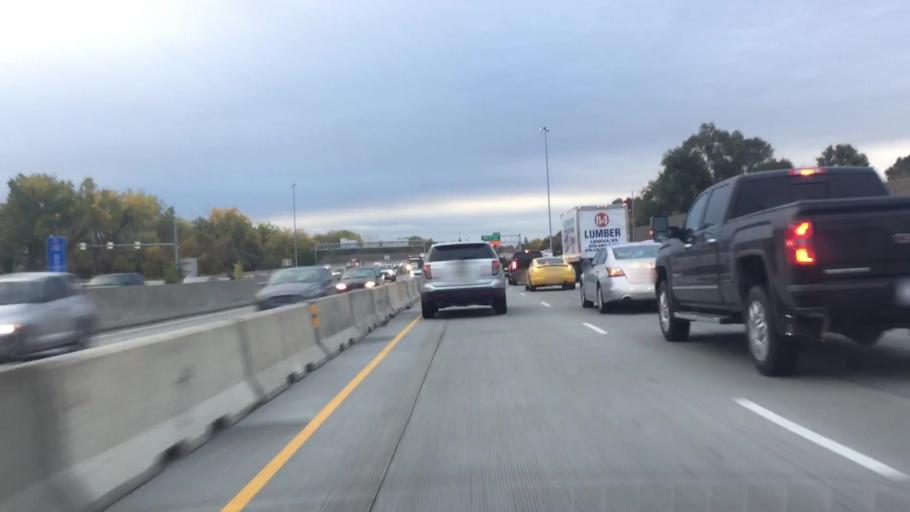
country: US
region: Kansas
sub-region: Johnson County
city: Lenexa
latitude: 38.9365
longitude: -94.6899
